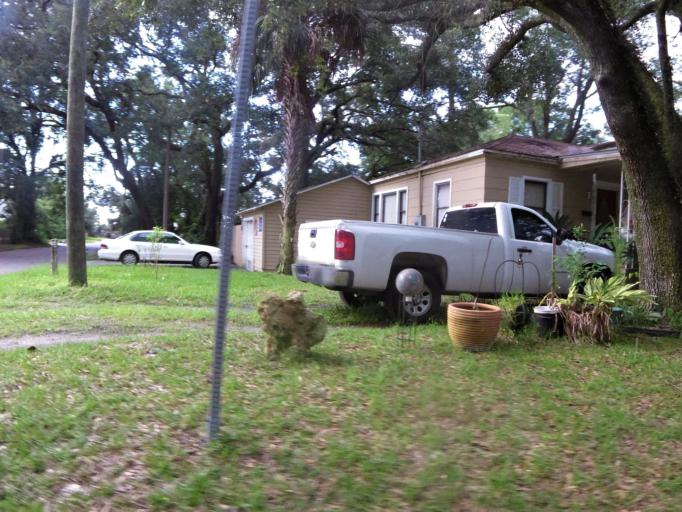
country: US
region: Florida
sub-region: Duval County
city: Jacksonville
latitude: 30.3473
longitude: -81.6317
